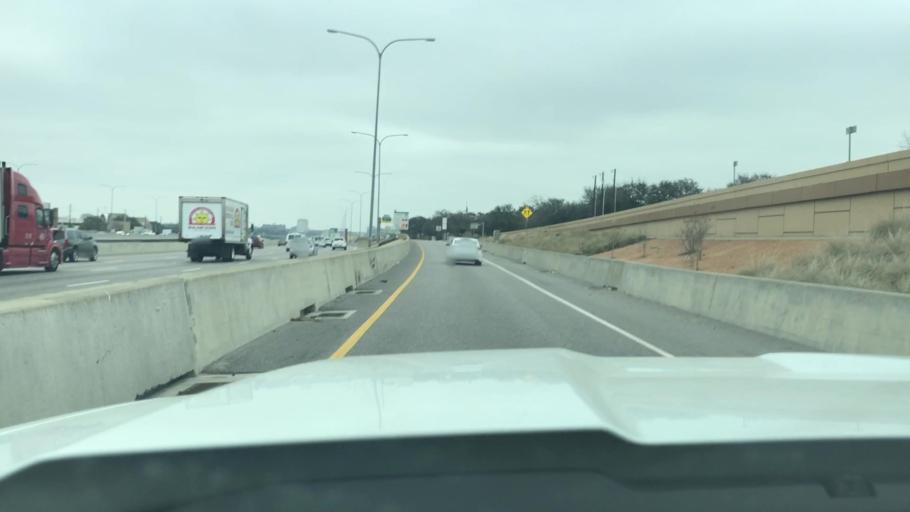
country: US
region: Texas
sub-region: Dallas County
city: Addison
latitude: 32.9247
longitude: -96.8006
